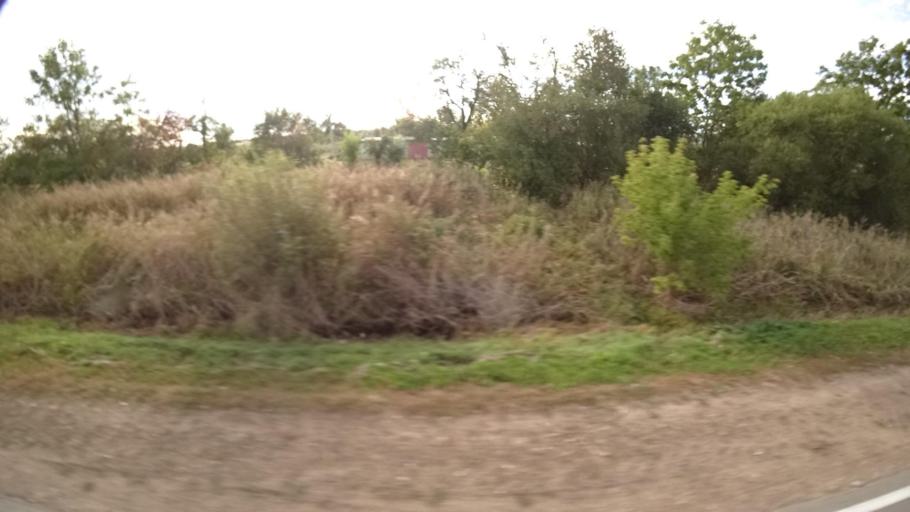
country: RU
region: Primorskiy
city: Dostoyevka
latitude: 44.2878
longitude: 133.4265
